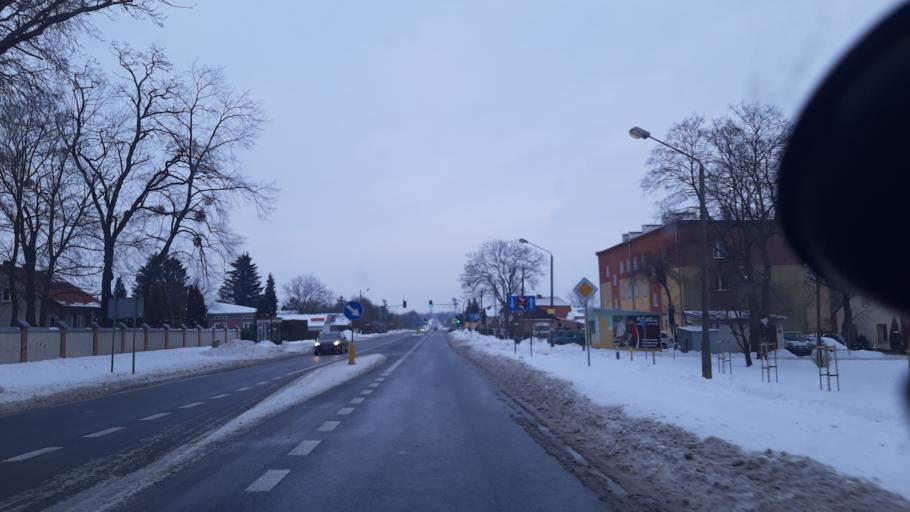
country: PL
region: Lublin Voivodeship
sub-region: Powiat lubelski
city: Garbow
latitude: 51.3642
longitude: 22.2983
